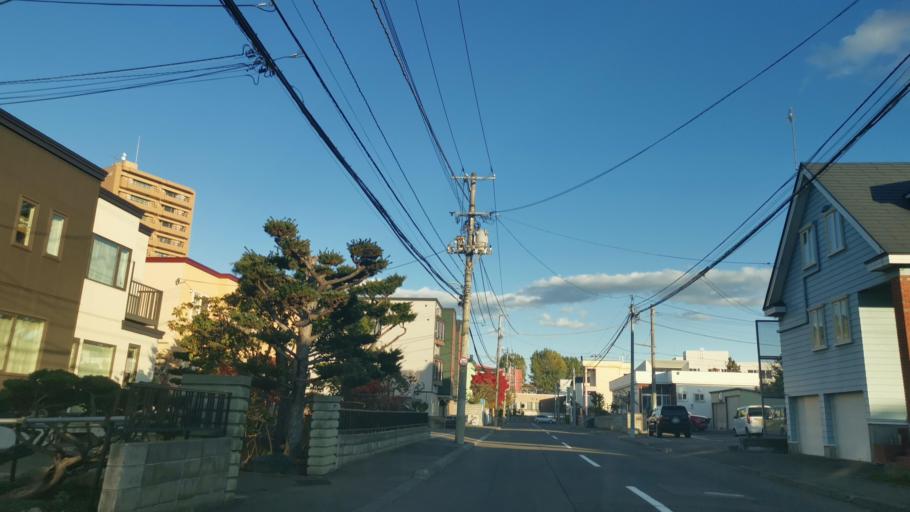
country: JP
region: Hokkaido
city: Sapporo
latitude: 43.0134
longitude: 141.3686
